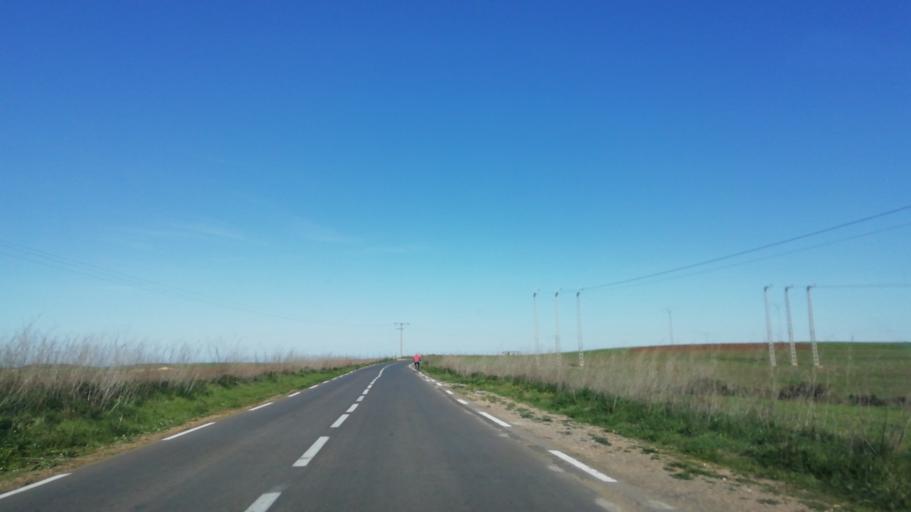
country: DZ
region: Oran
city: Bou Tlelis
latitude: 35.6437
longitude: -0.9448
